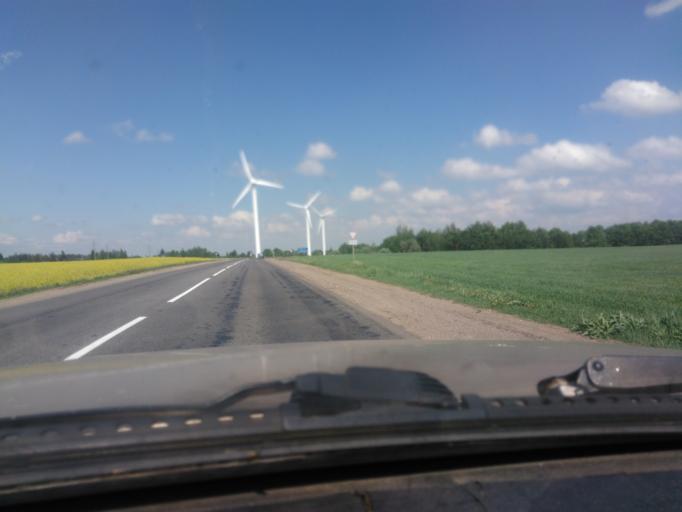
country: BY
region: Mogilev
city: Palykavichy Pyershyya
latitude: 53.9770
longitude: 30.3489
